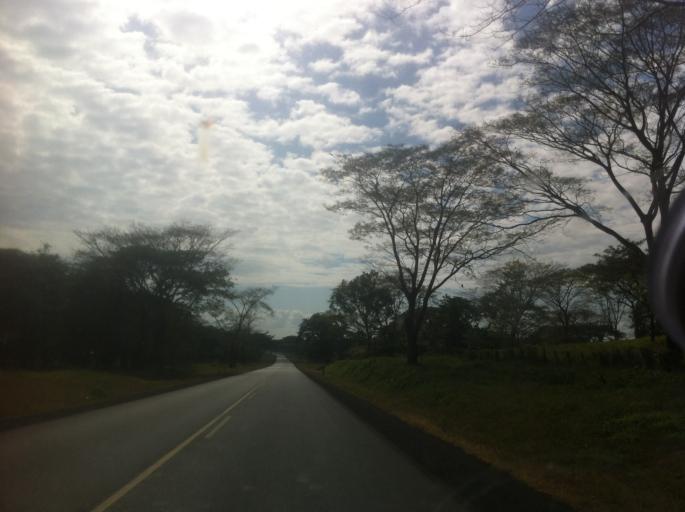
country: NI
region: Rio San Juan
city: San Miguelito
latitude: 11.3750
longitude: -84.7804
